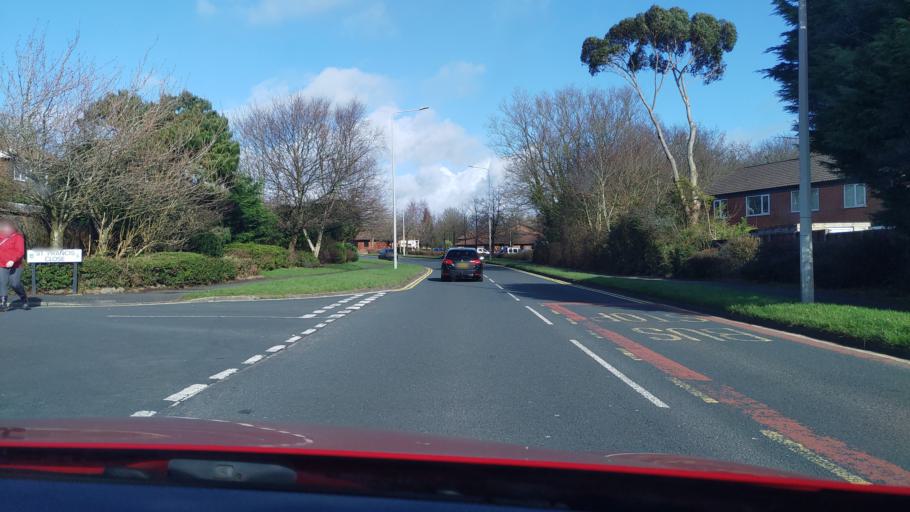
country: GB
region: England
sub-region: Lancashire
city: Preston
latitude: 53.7910
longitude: -2.6970
